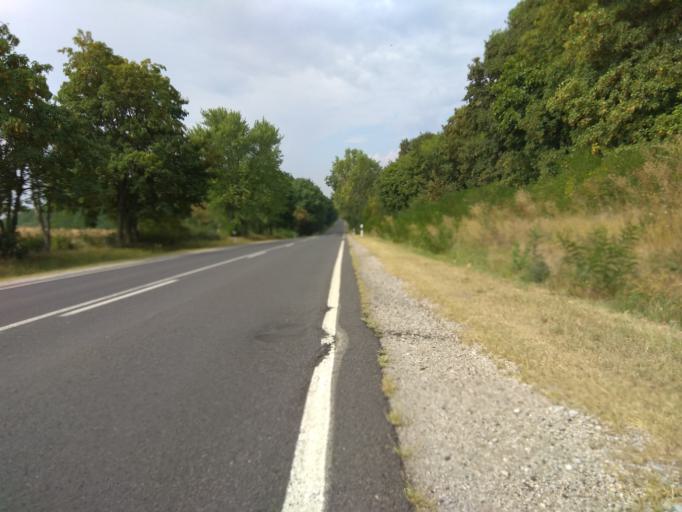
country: HU
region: Borsod-Abauj-Zemplen
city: Emod
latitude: 47.9279
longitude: 20.7863
